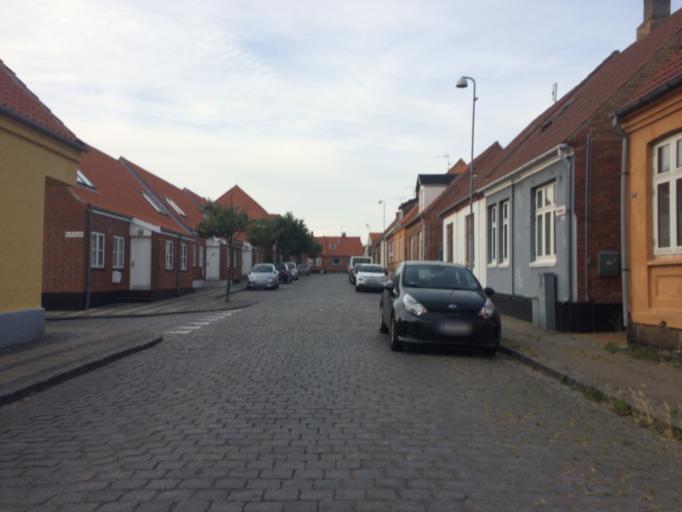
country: DK
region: Capital Region
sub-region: Bornholm Kommune
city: Ronne
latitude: 55.0988
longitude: 14.7065
